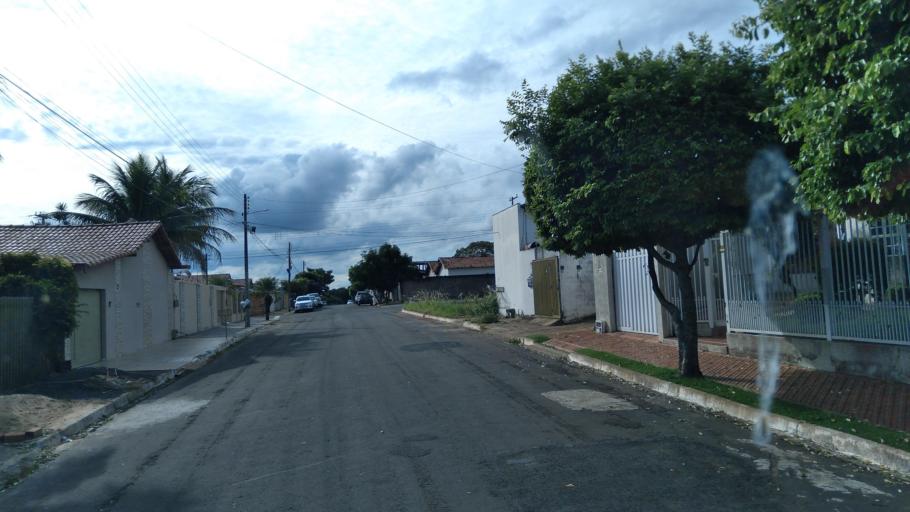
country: BR
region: Goias
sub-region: Mineiros
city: Mineiros
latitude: -17.5618
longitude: -52.5657
